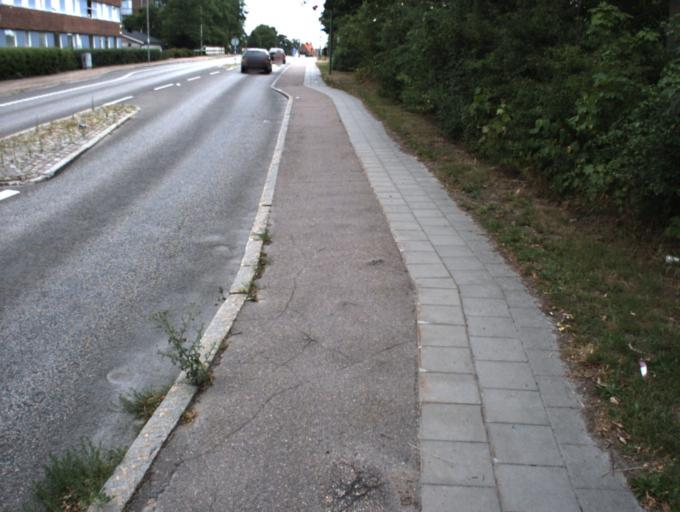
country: SE
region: Skane
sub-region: Helsingborg
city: Helsingborg
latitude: 56.0607
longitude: 12.7016
